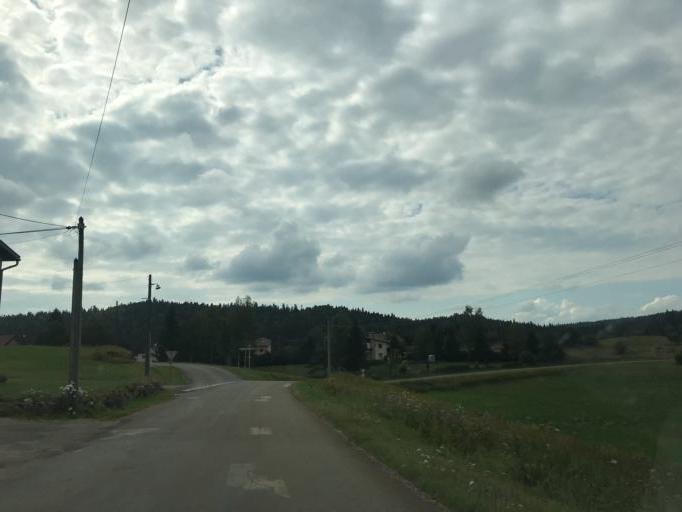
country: FR
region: Franche-Comte
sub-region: Departement du Jura
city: Longchaumois
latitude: 46.5110
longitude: 5.8737
